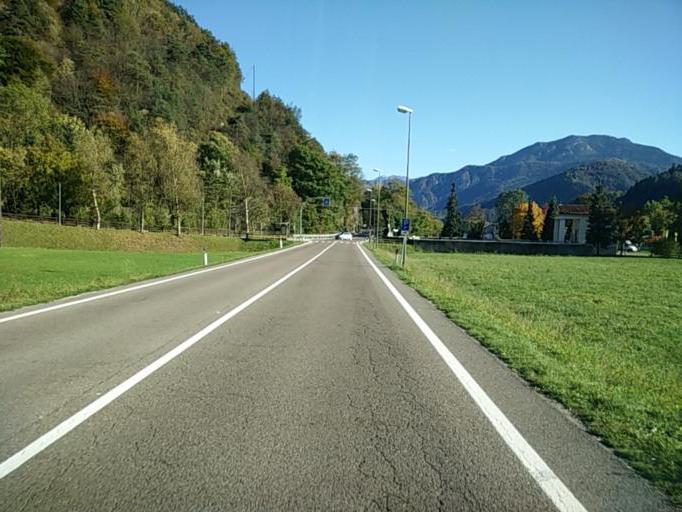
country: IT
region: Trentino-Alto Adige
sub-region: Provincia di Trento
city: Pieve di Ledro
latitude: 45.8877
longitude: 10.7336
